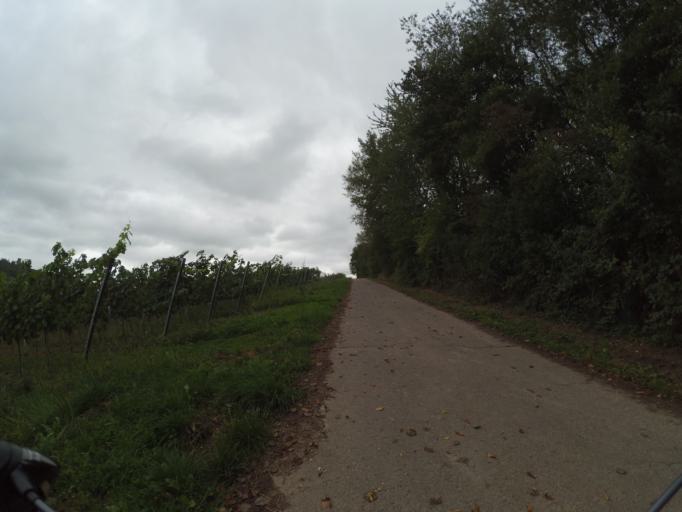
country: DE
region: Rheinland-Pfalz
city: Thornich
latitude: 49.8363
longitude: 6.8252
